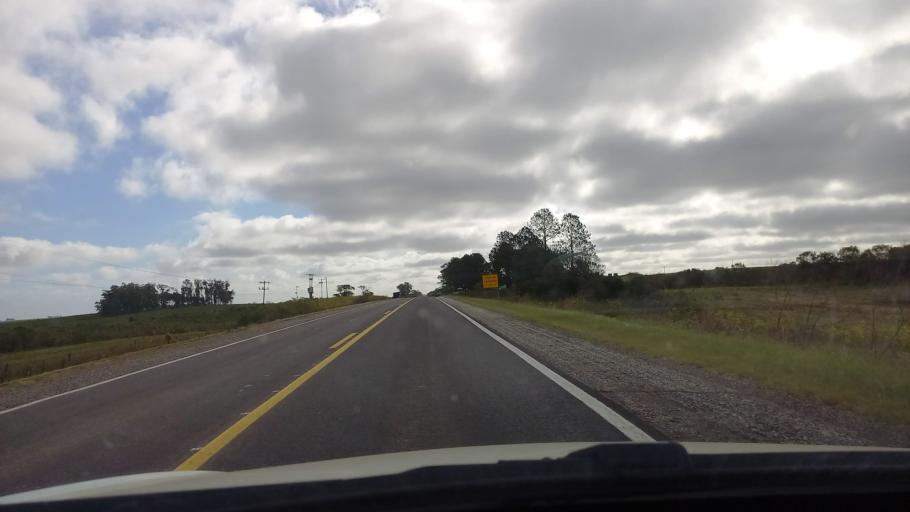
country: BR
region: Rio Grande do Sul
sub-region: Dom Pedrito
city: Dom Pedrito
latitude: -30.9032
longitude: -54.8292
